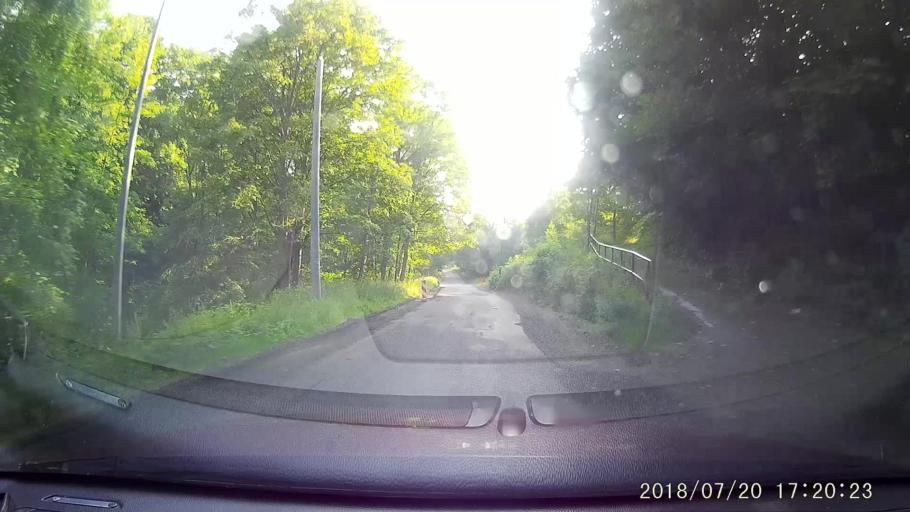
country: PL
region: Lower Silesian Voivodeship
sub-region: Powiat lubanski
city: Lesna
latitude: 50.9882
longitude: 15.2897
